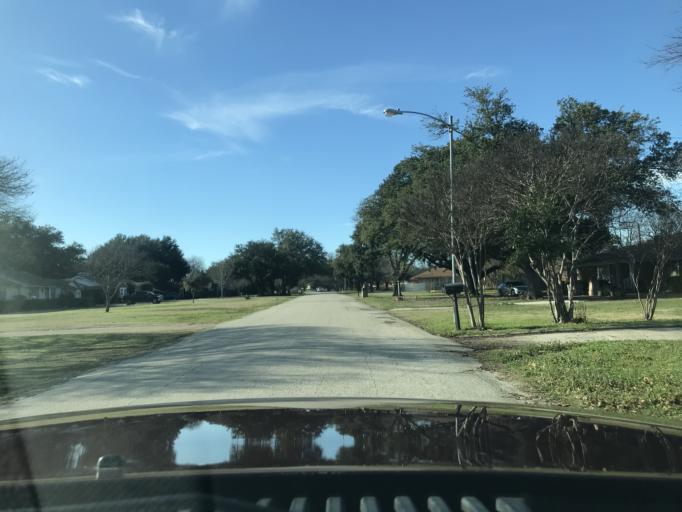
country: US
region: Texas
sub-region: Tarrant County
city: Edgecliff Village
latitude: 32.6580
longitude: -97.3436
